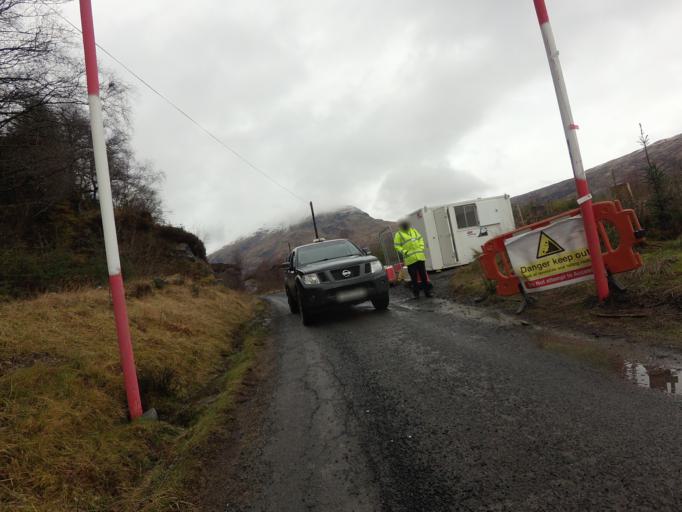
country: GB
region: Scotland
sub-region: West Dunbartonshire
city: Balloch
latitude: 56.2611
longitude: -4.5796
